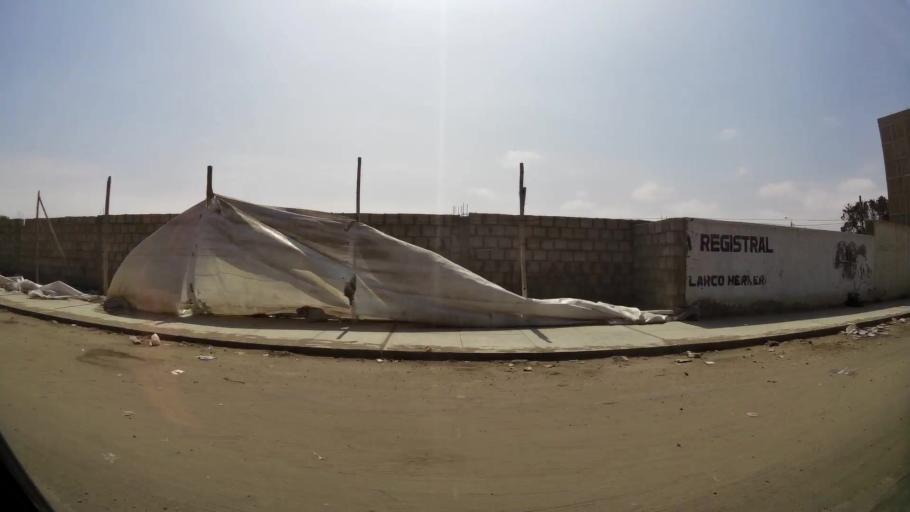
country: PE
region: La Libertad
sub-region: Provincia de Trujillo
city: Buenos Aires
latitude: -8.1264
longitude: -79.0465
